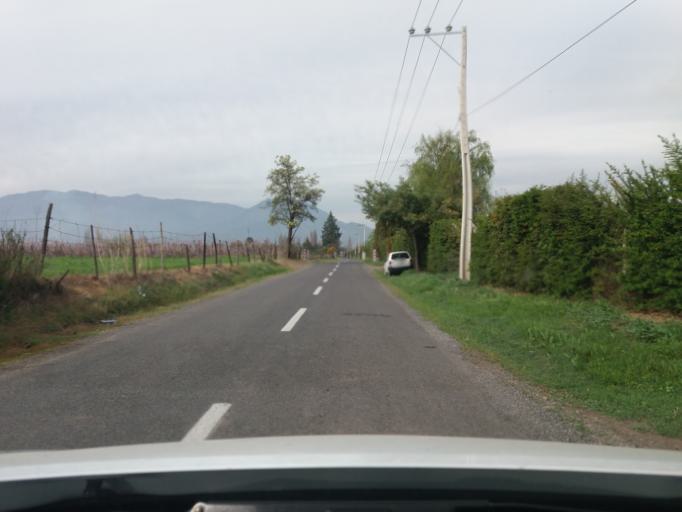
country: CL
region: Valparaiso
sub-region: Provincia de Los Andes
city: Los Andes
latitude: -32.8315
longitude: -70.6600
